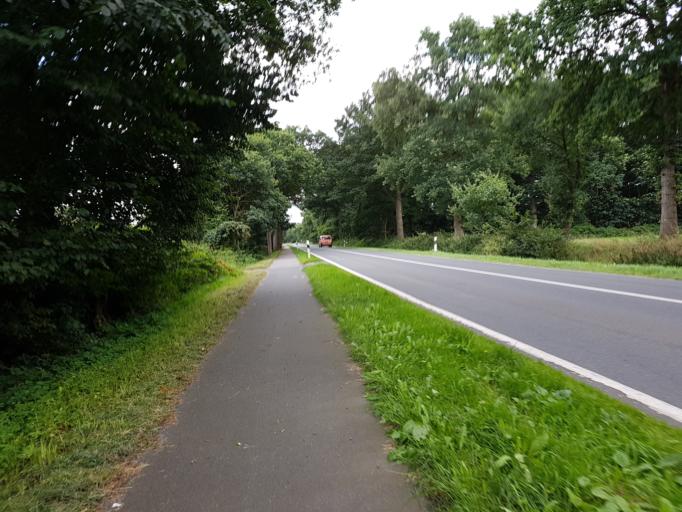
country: DE
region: Lower Saxony
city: Wittmund
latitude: 53.5163
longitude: 7.7932
